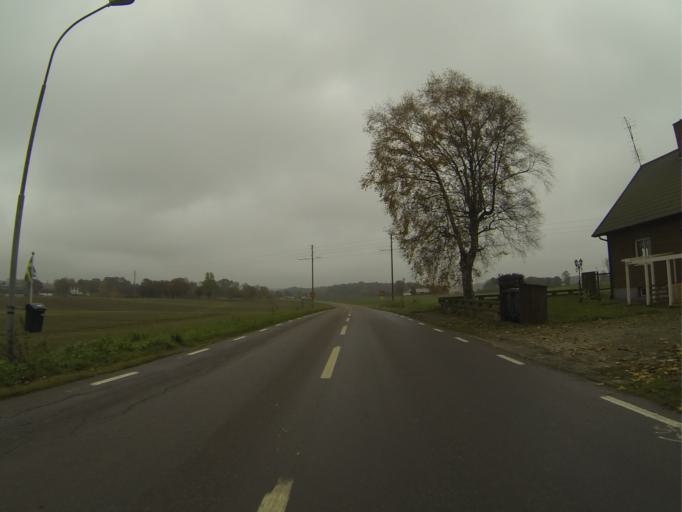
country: SE
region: Skane
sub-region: Tomelilla Kommun
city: Tomelilla
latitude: 55.6092
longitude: 13.9231
